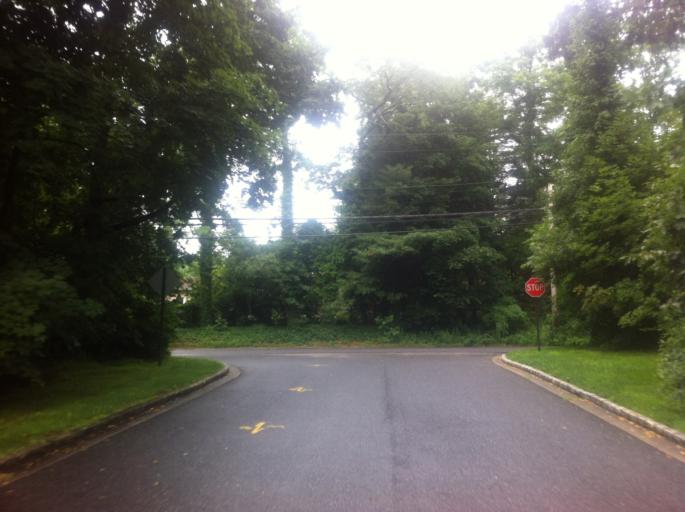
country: US
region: New York
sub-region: Nassau County
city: Jericho
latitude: 40.8088
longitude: -73.5403
